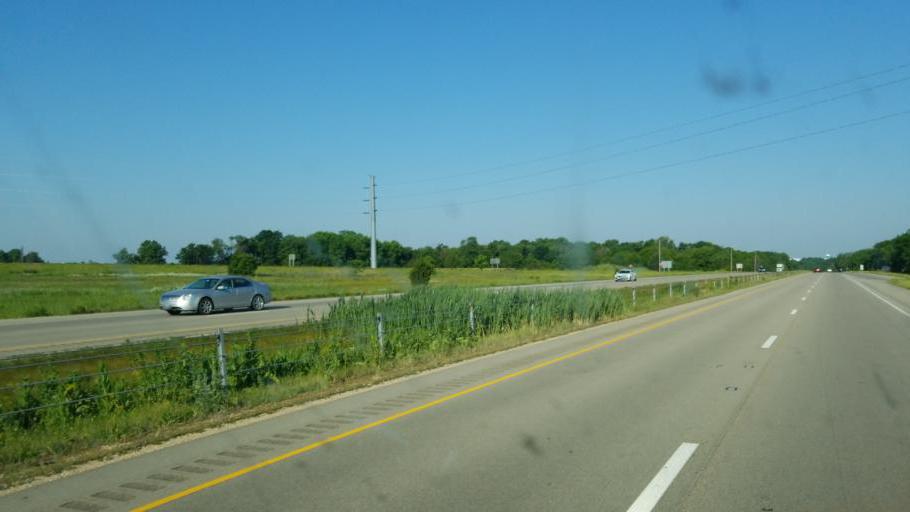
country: US
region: Illinois
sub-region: LaSalle County
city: Ottawa
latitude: 41.3767
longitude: -88.7797
